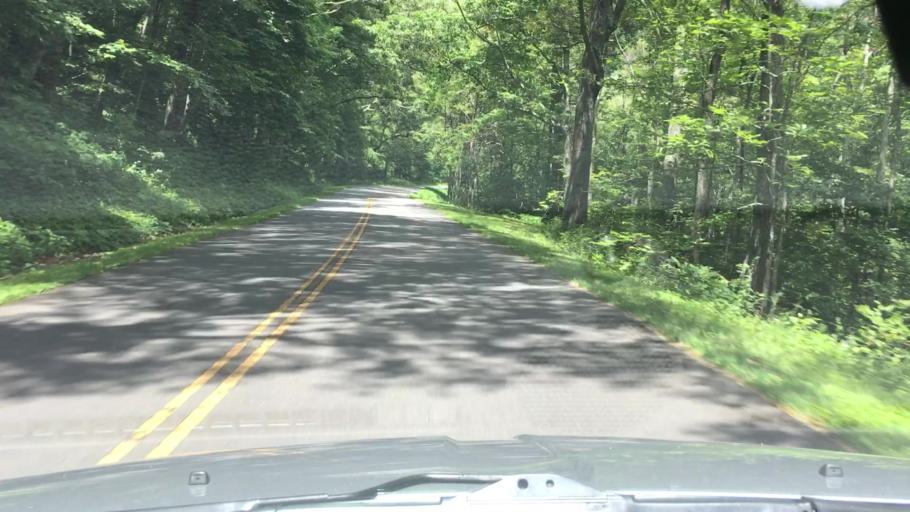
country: US
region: North Carolina
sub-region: Buncombe County
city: Swannanoa
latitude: 35.6738
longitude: -82.4429
